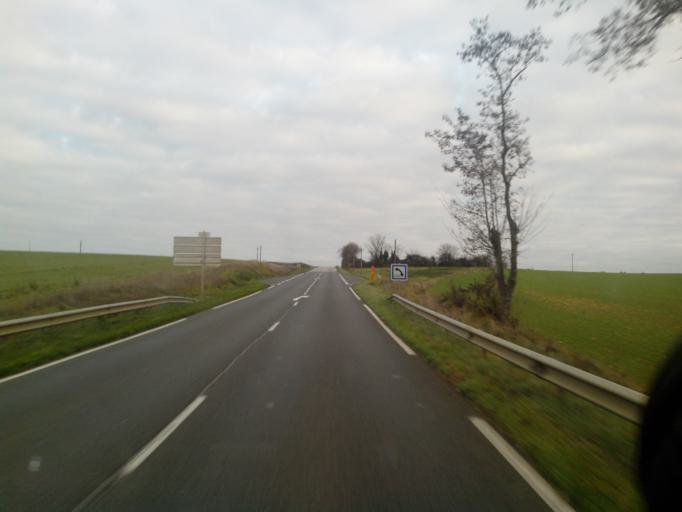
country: FR
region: Poitou-Charentes
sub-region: Departement de la Vienne
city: Ayron
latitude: 46.6535
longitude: 0.1196
